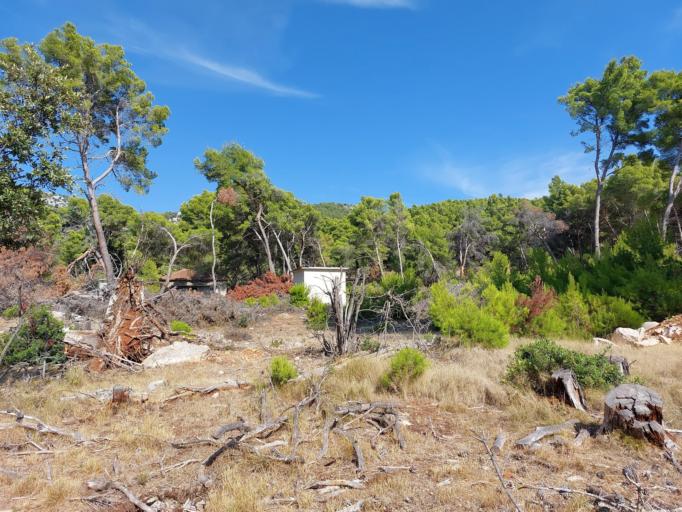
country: HR
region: Dubrovacko-Neretvanska
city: Smokvica
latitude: 42.7378
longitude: 16.8275
